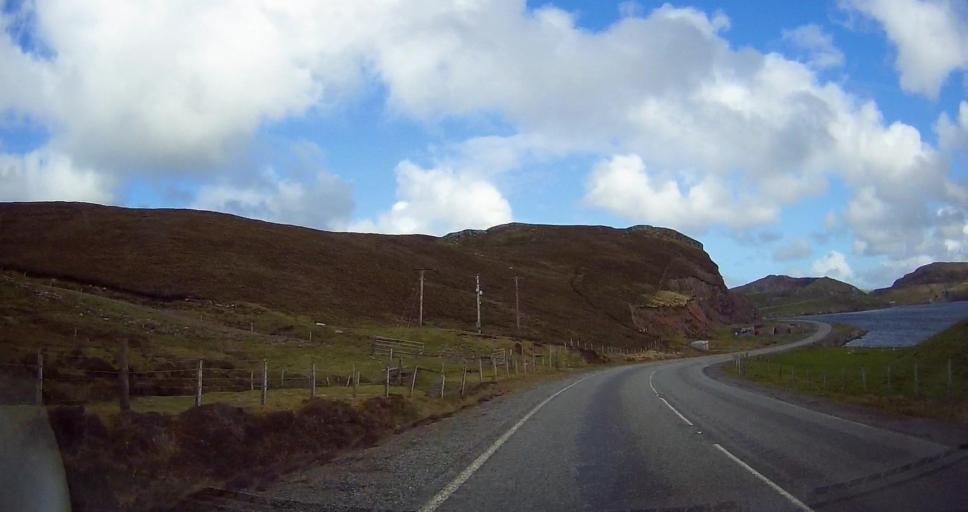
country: GB
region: Scotland
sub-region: Shetland Islands
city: Lerwick
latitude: 60.3922
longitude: -1.3764
